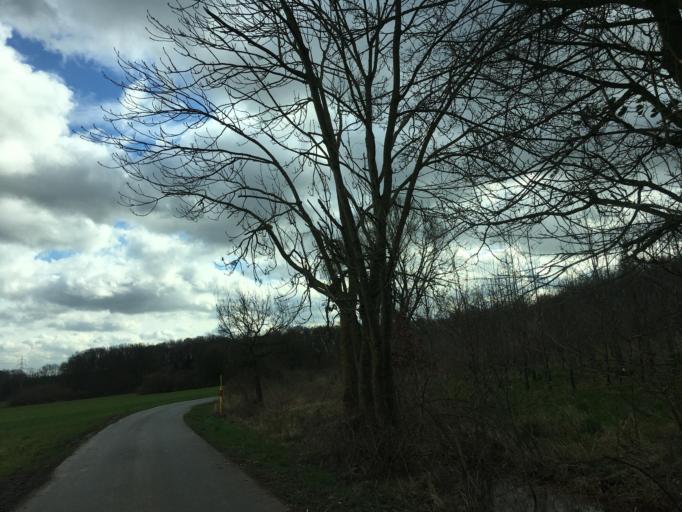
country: DE
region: North Rhine-Westphalia
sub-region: Regierungsbezirk Munster
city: Horstmar
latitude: 52.0960
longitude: 7.3114
